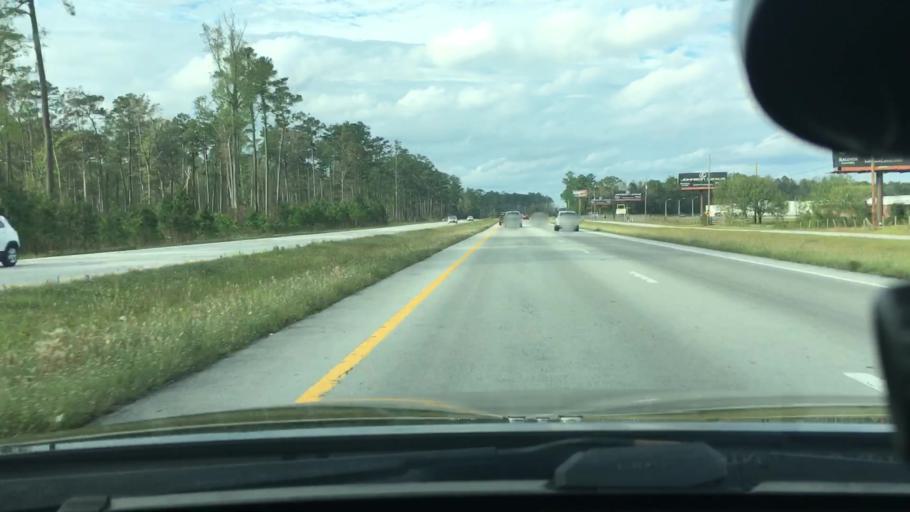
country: US
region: North Carolina
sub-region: Craven County
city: Neuse Forest
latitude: 34.9335
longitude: -76.9490
